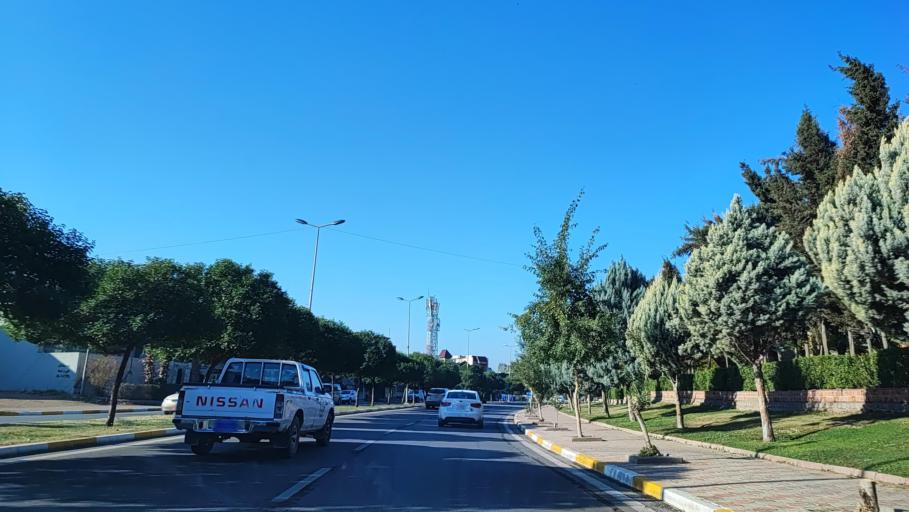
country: IQ
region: Arbil
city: Erbil
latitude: 36.1798
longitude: 44.0052
